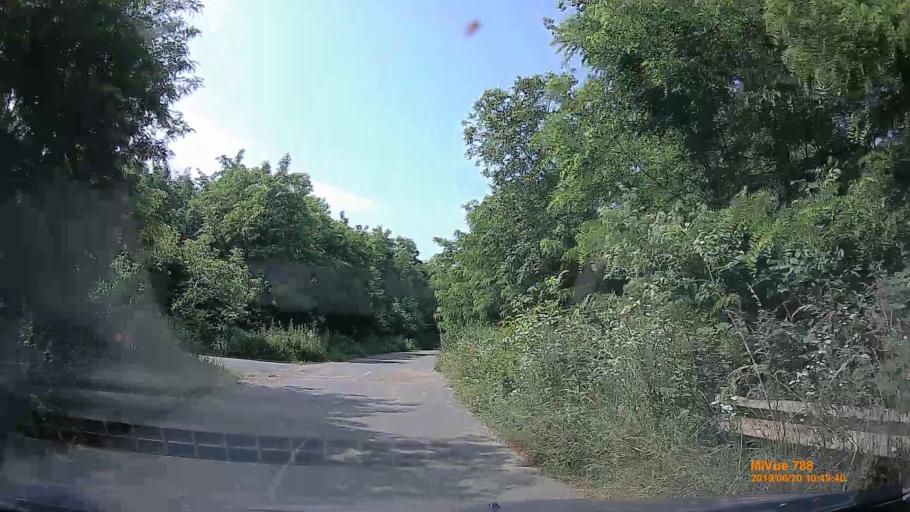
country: HU
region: Baranya
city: Mecseknadasd
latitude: 46.1608
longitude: 18.5830
